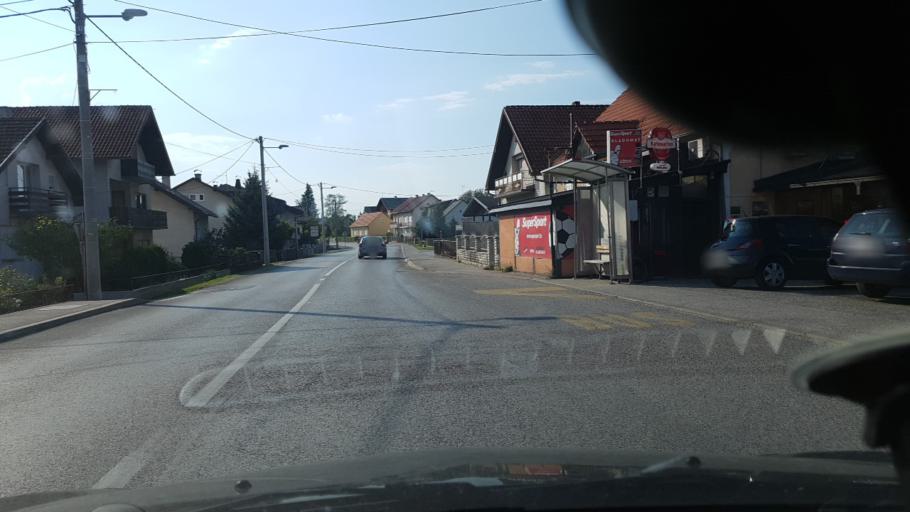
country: HR
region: Zagrebacka
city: Brdovec
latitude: 45.8660
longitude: 15.7661
